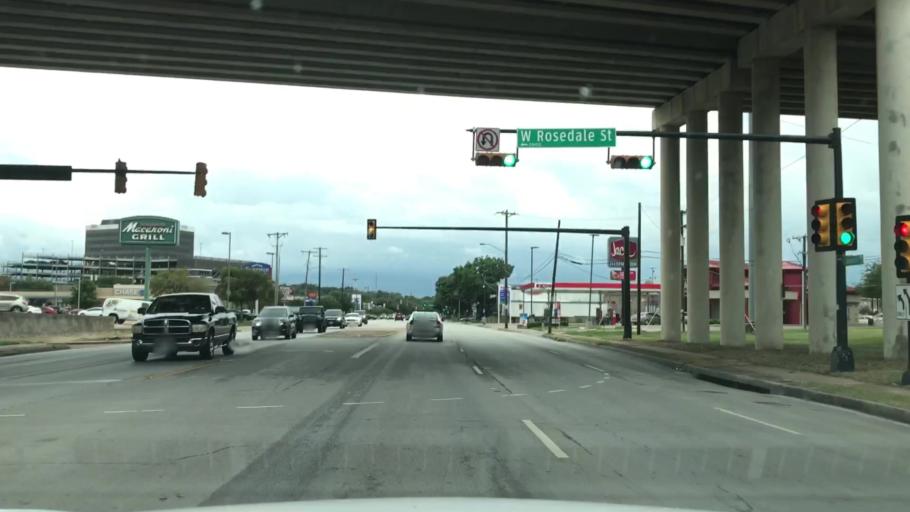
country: US
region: Texas
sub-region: Tarrant County
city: Fort Worth
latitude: 32.7312
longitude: -97.3615
